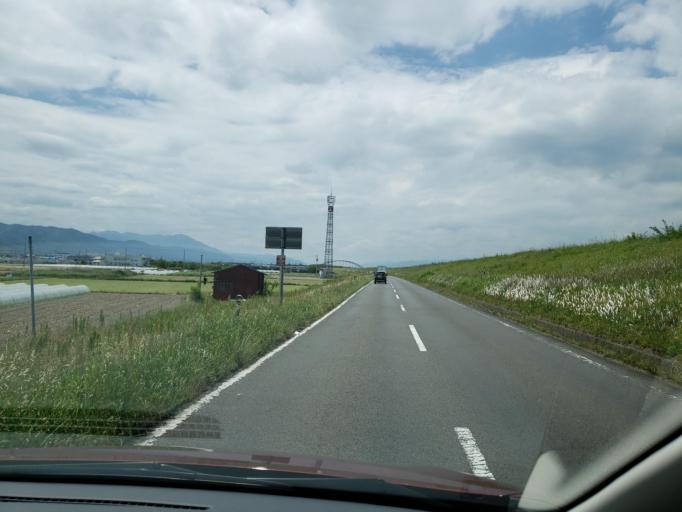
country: JP
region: Tokushima
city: Ishii
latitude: 34.0897
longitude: 134.4020
